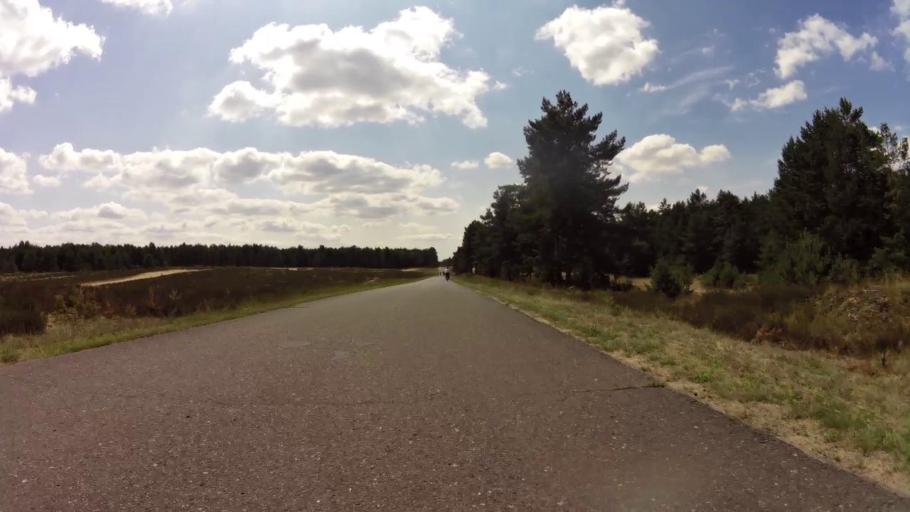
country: PL
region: West Pomeranian Voivodeship
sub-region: Powiat drawski
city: Drawsko Pomorskie
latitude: 53.4106
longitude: 15.7366
